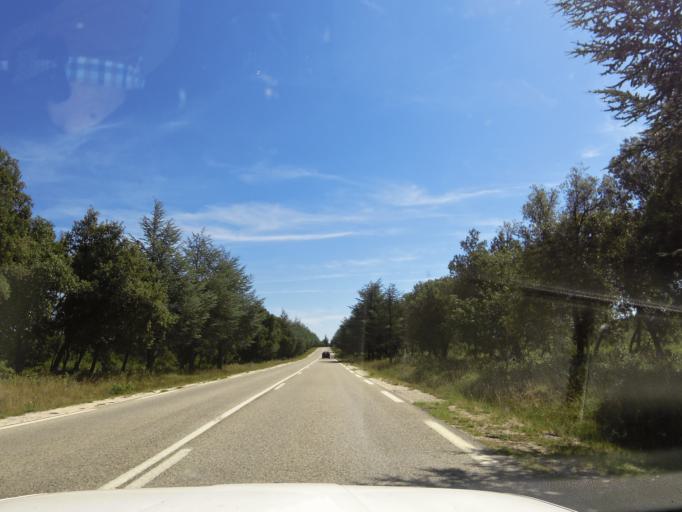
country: FR
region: Languedoc-Roussillon
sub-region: Departement du Gard
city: Saint-Quentin-la-Poterie
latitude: 44.1288
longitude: 4.4422
